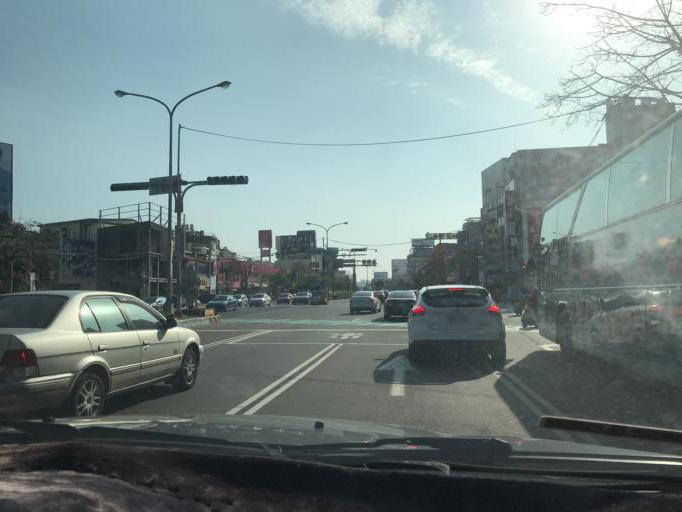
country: TW
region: Taiwan
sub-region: Hsinchu
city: Zhubei
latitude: 24.8174
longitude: 121.0261
